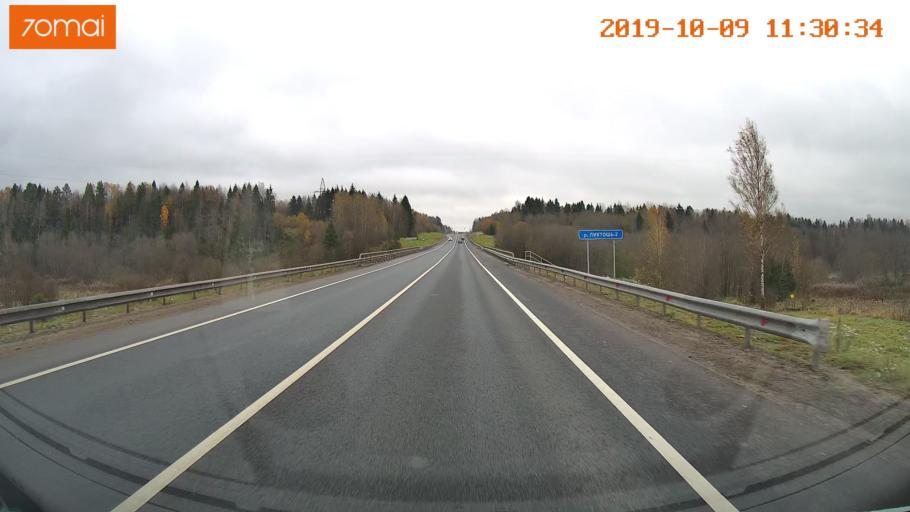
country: RU
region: Vologda
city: Gryazovets
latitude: 59.0526
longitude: 40.0782
